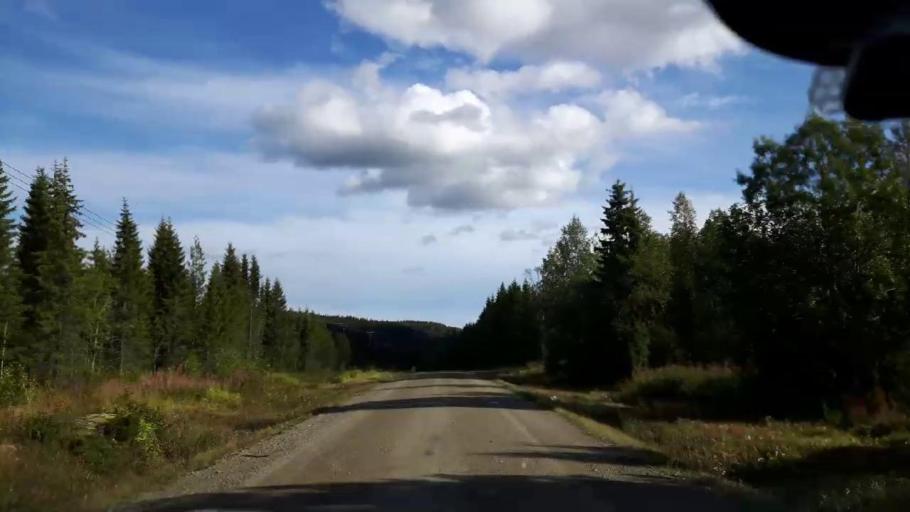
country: SE
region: Jaemtland
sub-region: Ragunda Kommun
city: Hammarstrand
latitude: 63.4255
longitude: 16.0579
